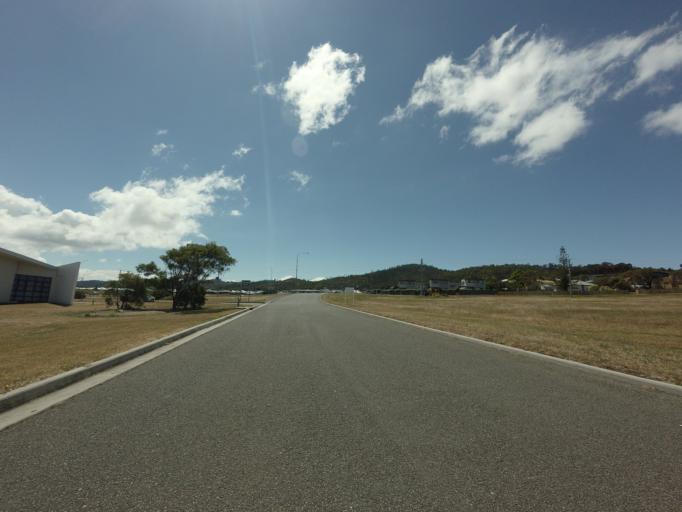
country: AU
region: Tasmania
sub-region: Clarence
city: Rokeby
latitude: -42.9068
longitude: 147.4543
